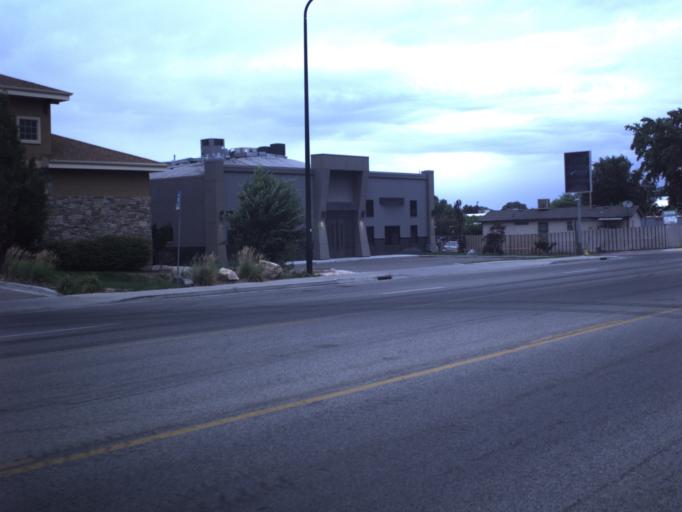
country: US
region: Utah
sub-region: Weber County
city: Ogden
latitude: 41.2458
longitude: -111.9781
